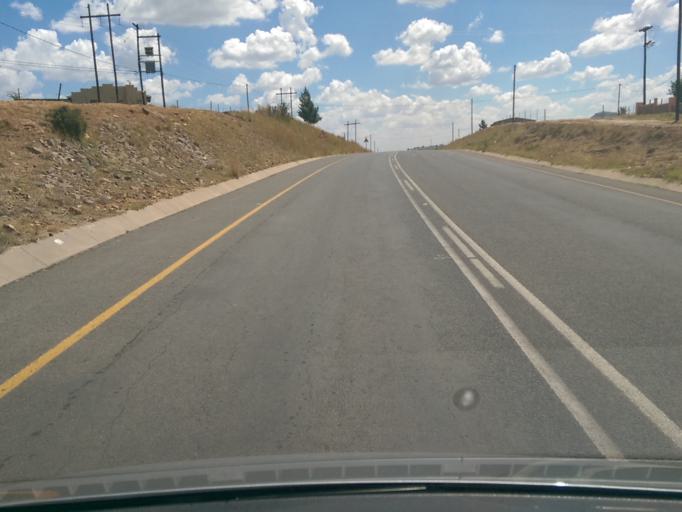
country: LS
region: Maseru
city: Maseru
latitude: -29.3965
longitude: 27.5208
